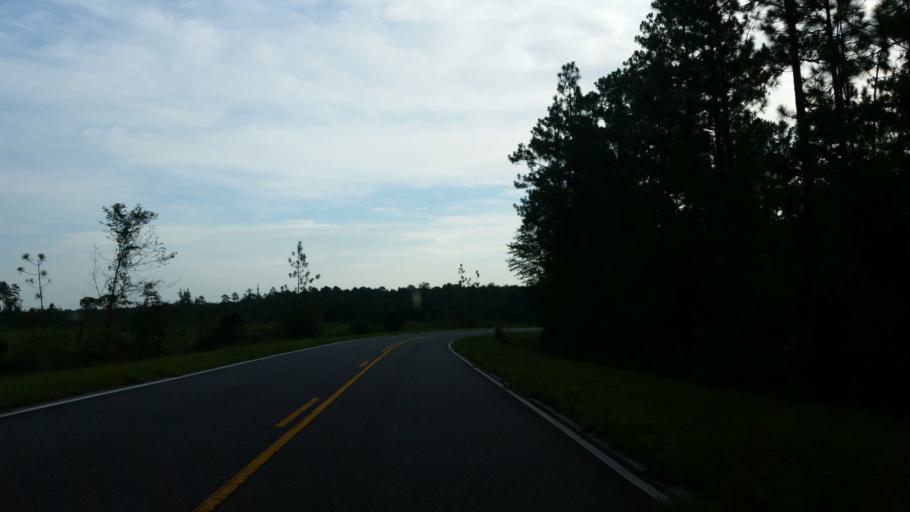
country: US
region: Florida
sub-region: Escambia County
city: Molino
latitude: 30.7733
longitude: -87.4966
